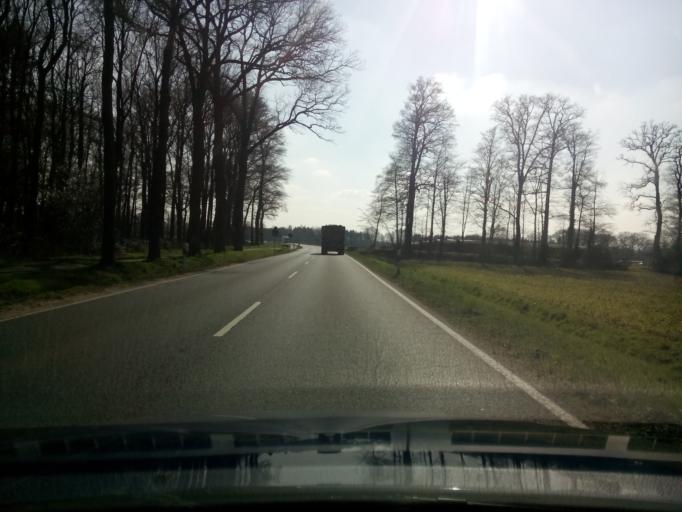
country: DE
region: Lower Saxony
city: Isterberg
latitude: 52.3317
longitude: 7.0676
